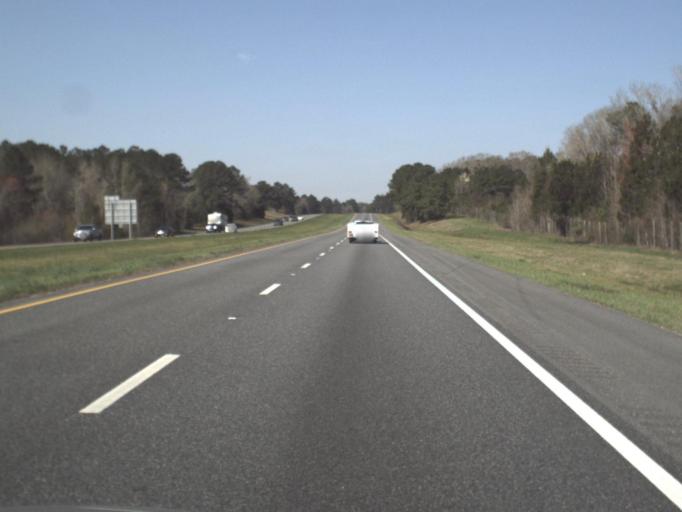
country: US
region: Florida
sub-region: Jackson County
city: Marianna
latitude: 30.7266
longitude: -85.2094
